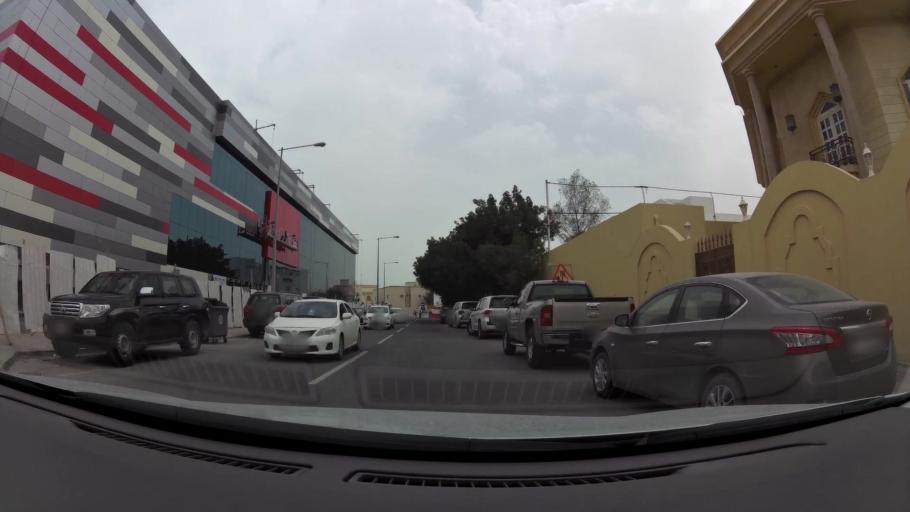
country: QA
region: Baladiyat ad Dawhah
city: Doha
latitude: 25.2593
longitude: 51.5103
